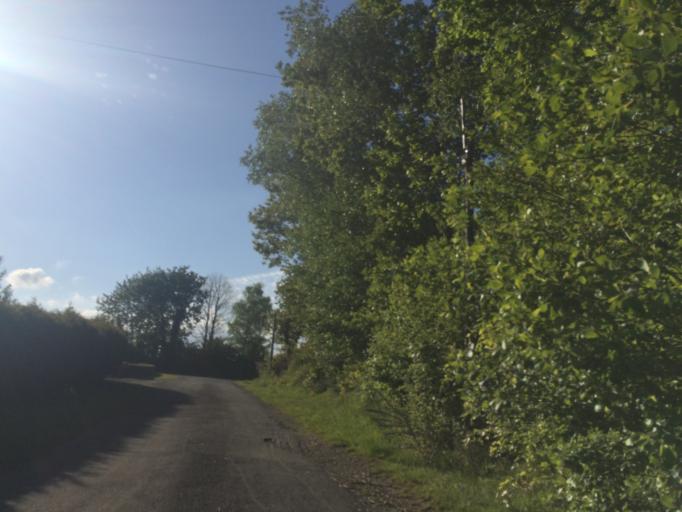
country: FR
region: Brittany
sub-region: Departement du Finistere
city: Daoulas
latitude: 48.3595
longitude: -4.2540
